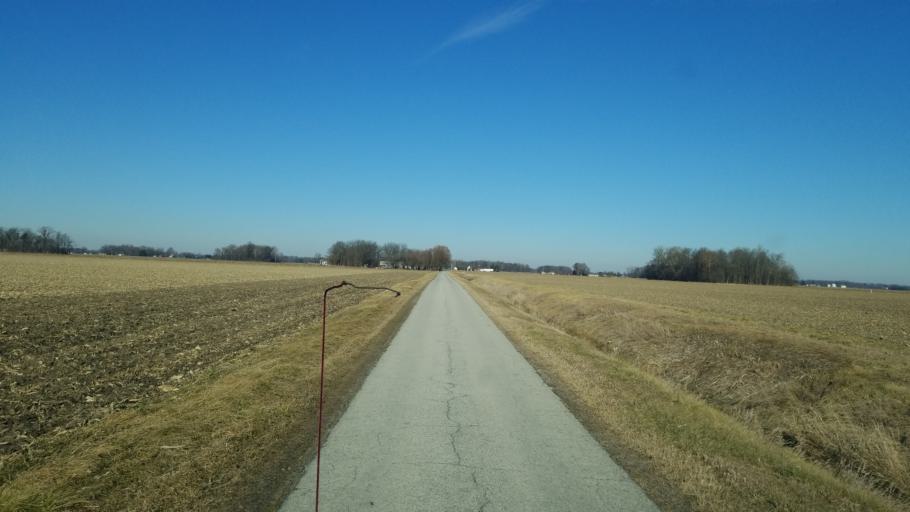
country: US
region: Ohio
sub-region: Henry County
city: Liberty Center
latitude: 41.3609
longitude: -83.9802
